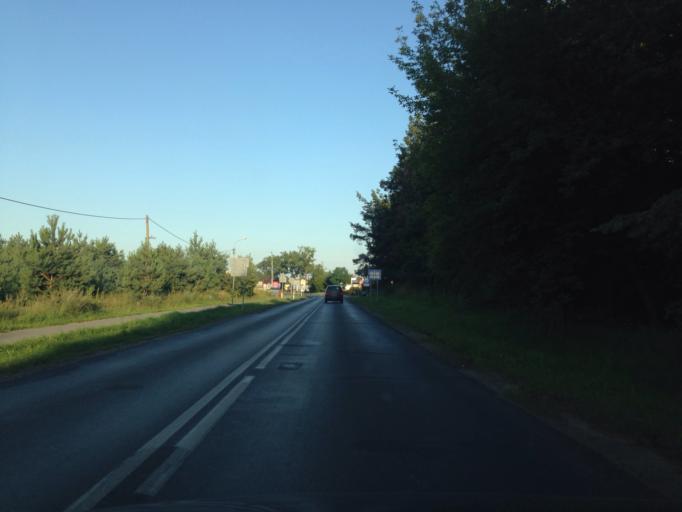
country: PL
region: Kujawsko-Pomorskie
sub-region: Powiat aleksandrowski
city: Aleksandrow Kujawski
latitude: 52.8651
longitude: 18.7192
